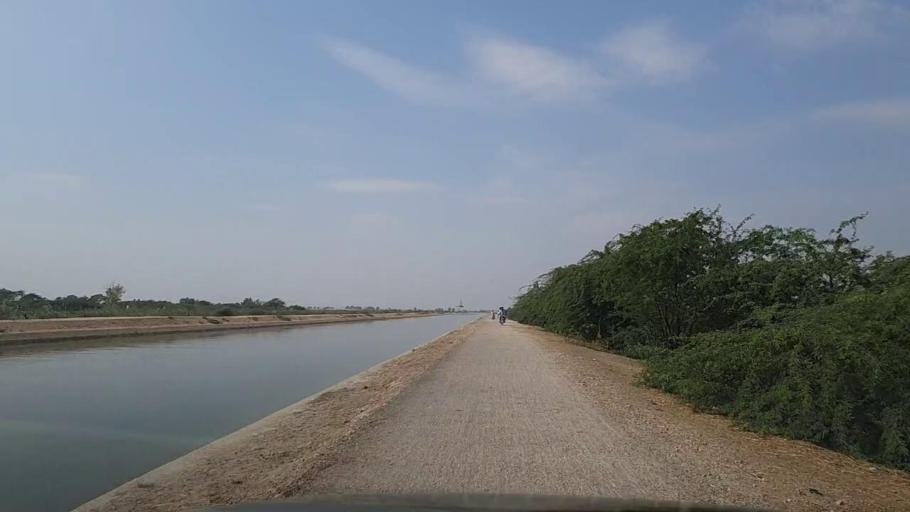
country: PK
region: Sindh
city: Thatta
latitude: 24.7543
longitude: 67.7657
